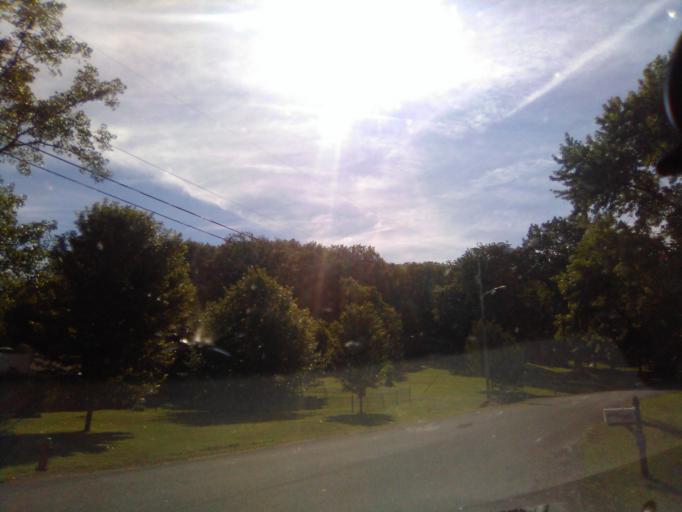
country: US
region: Tennessee
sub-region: Davidson County
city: Belle Meade
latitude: 36.1098
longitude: -86.9098
